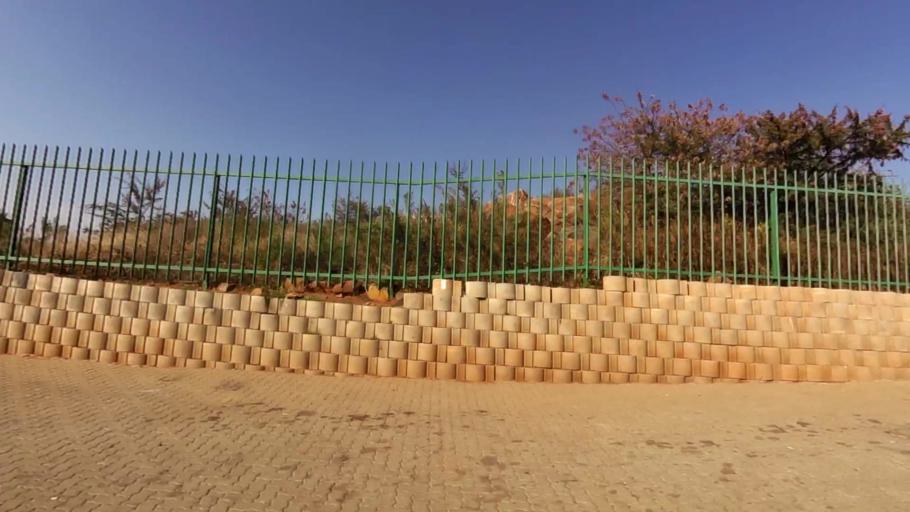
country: ZA
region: Gauteng
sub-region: City of Johannesburg Metropolitan Municipality
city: Soweto
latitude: -26.2967
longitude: 27.9479
